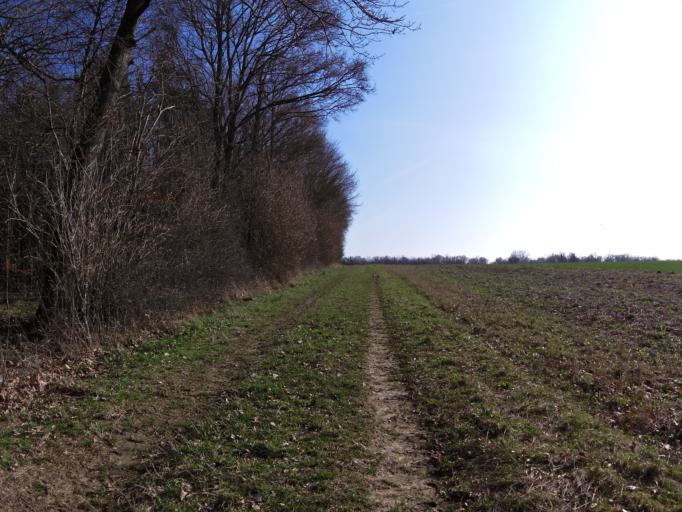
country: DE
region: Bavaria
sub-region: Regierungsbezirk Unterfranken
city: Rottendorf
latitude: 49.8209
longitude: 10.0400
